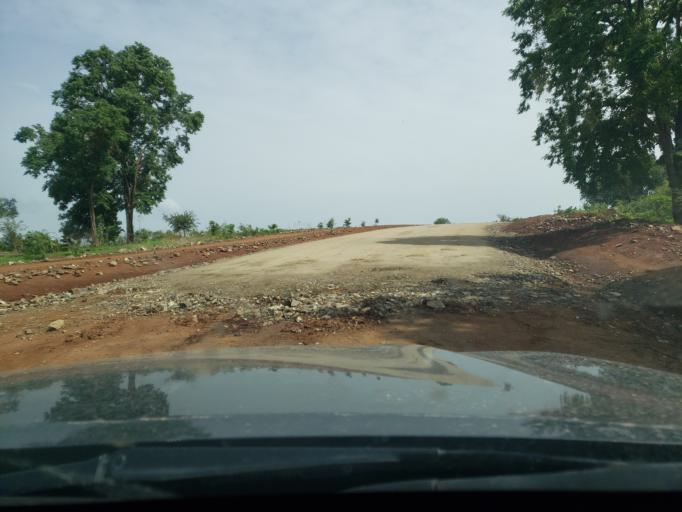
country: ET
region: Oromiya
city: Mendi
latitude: 10.1181
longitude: 35.1521
